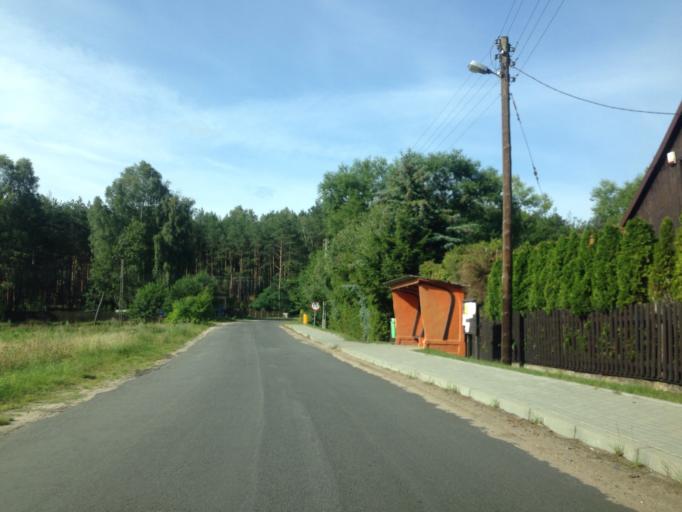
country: PL
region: Pomeranian Voivodeship
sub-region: Powiat starogardzki
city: Osiek
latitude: 53.7318
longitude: 18.4216
